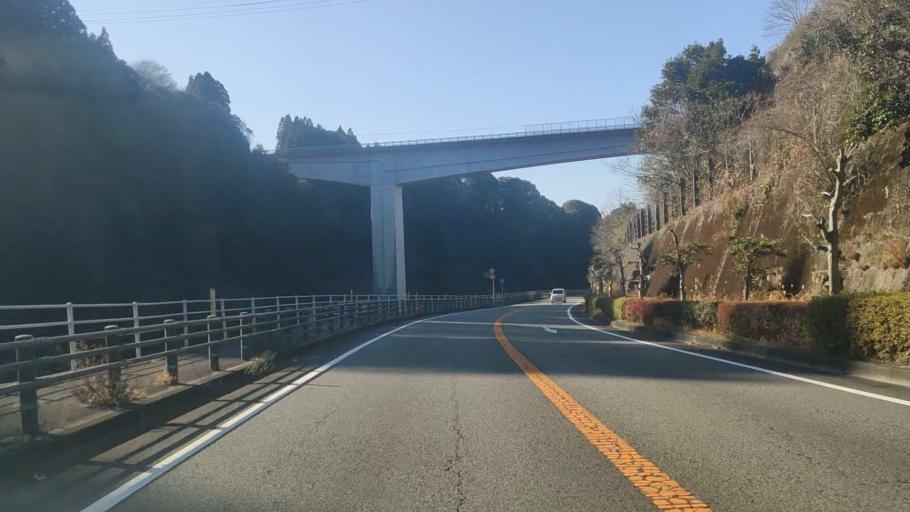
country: JP
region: Oita
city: Usuki
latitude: 33.0689
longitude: 131.6530
